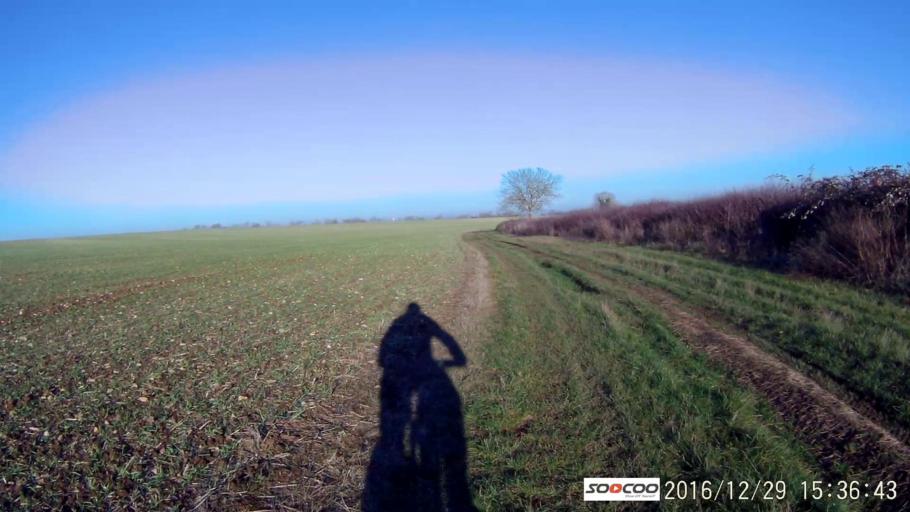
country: FR
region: Centre
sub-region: Departement de l'Indre
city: Neuvy-Pailloux
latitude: 46.9407
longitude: 1.8367
